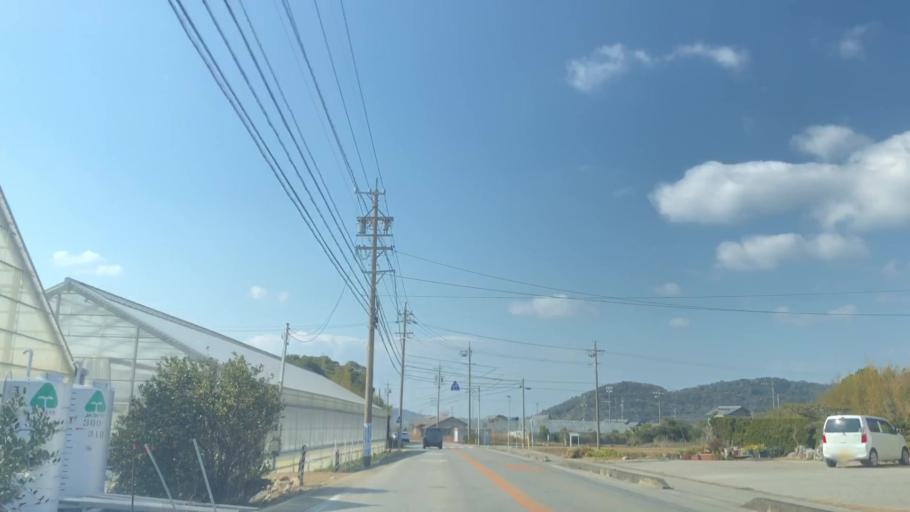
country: JP
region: Aichi
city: Tahara
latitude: 34.5915
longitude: 137.1026
